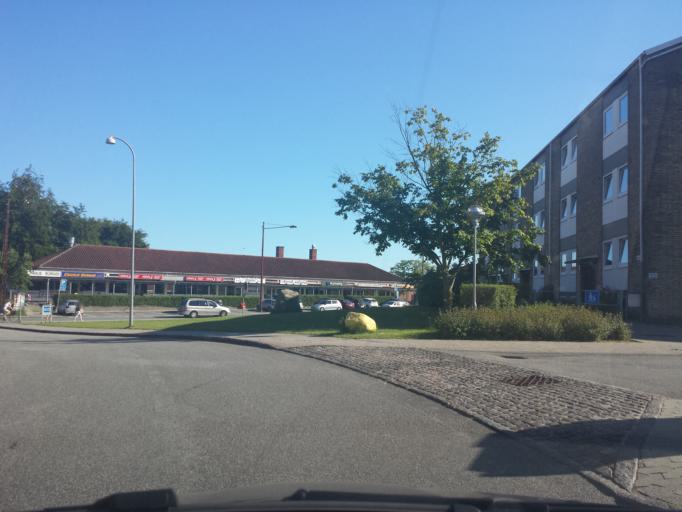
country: DK
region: Capital Region
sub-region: Herlev Kommune
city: Herlev
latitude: 55.7222
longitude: 12.4012
